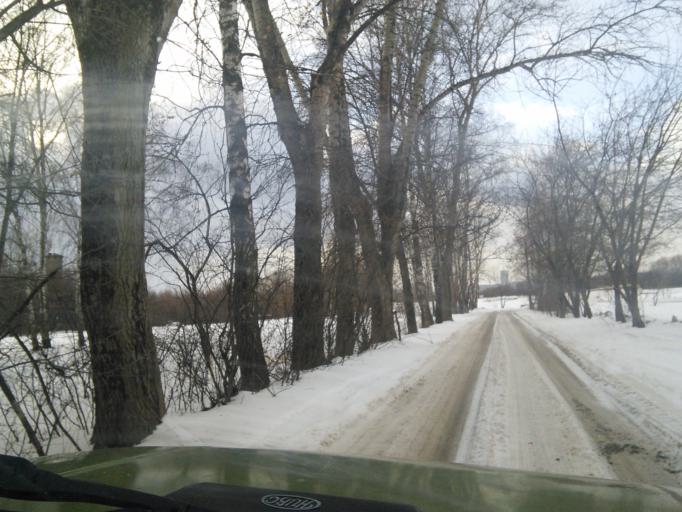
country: RU
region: Moskovskaya
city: Fili
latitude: 55.7555
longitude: 37.4748
